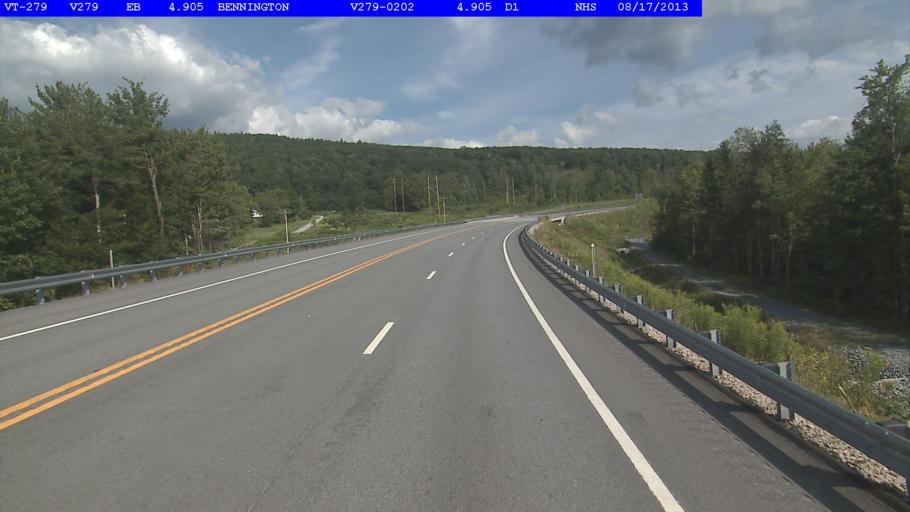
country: US
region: Vermont
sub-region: Bennington County
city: Bennington
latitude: 42.9015
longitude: -73.1817
